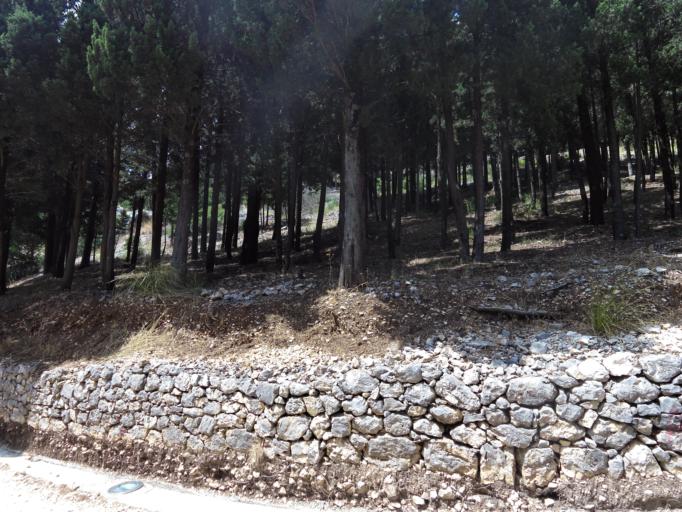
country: IT
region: Calabria
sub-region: Provincia di Reggio Calabria
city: Stilo
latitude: 38.4756
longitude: 16.4610
